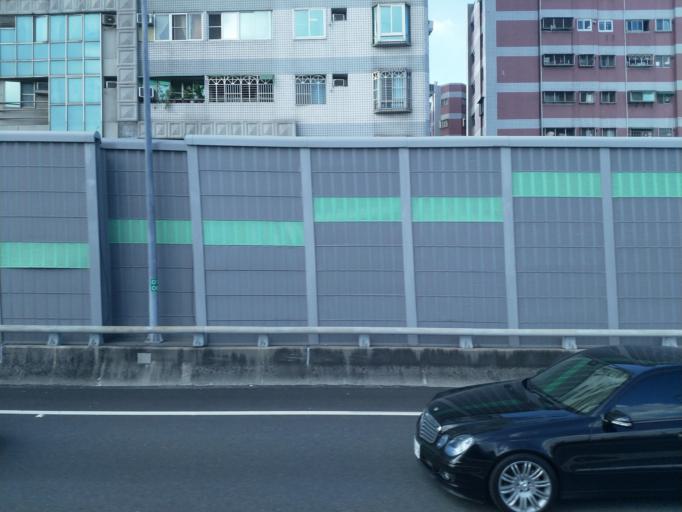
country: TW
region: Kaohsiung
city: Kaohsiung
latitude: 22.6763
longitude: 120.3238
